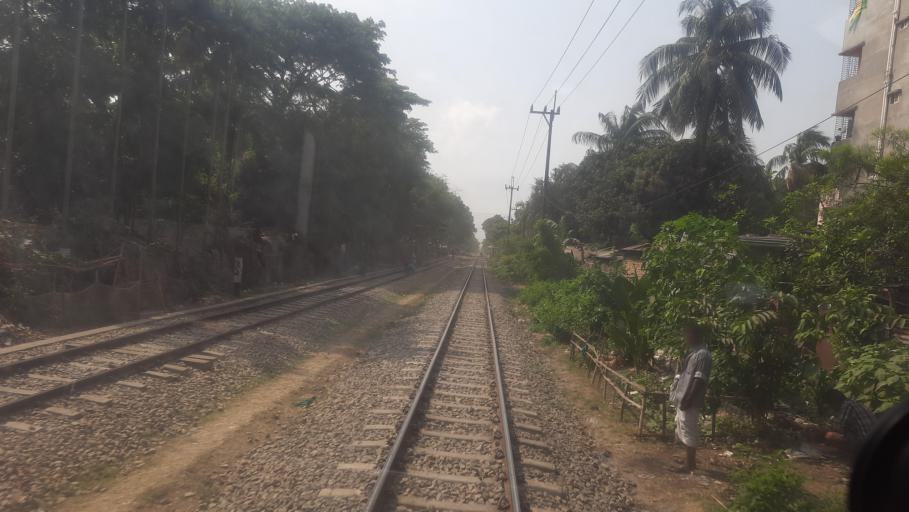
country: BD
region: Chittagong
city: Chittagong
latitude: 22.3655
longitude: 91.7834
